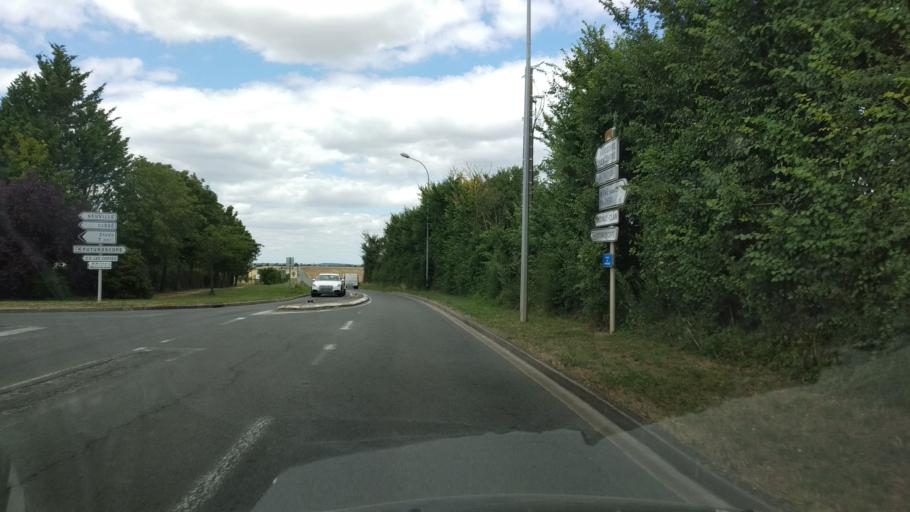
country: FR
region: Poitou-Charentes
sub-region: Departement de la Vienne
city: Avanton
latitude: 46.6656
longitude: 0.3047
